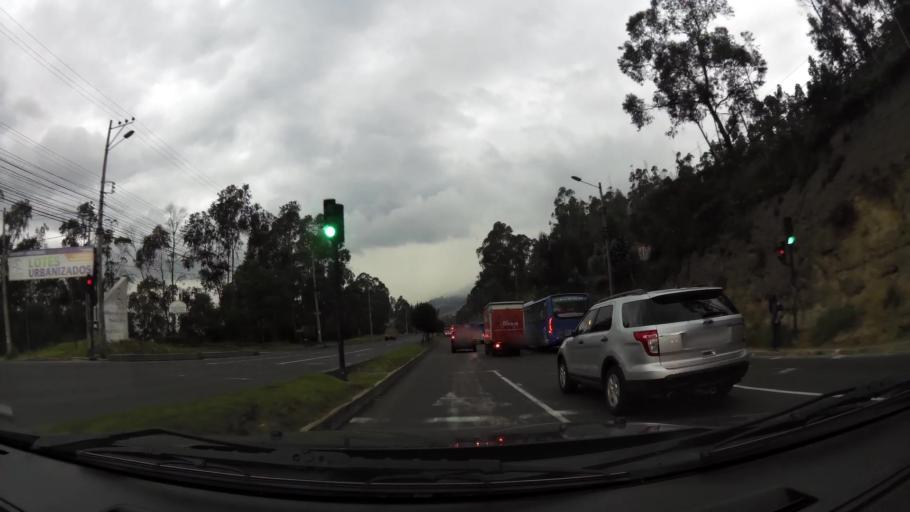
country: EC
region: Pichincha
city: Quito
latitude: -0.1003
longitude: -78.4639
